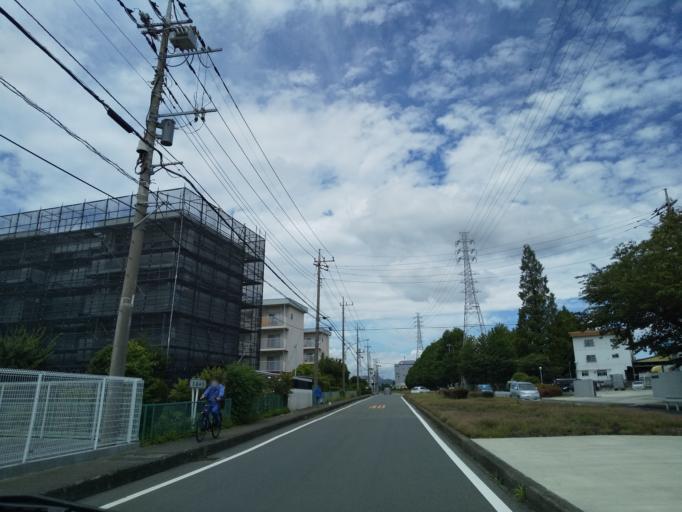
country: JP
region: Kanagawa
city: Zama
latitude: 35.5081
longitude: 139.3464
